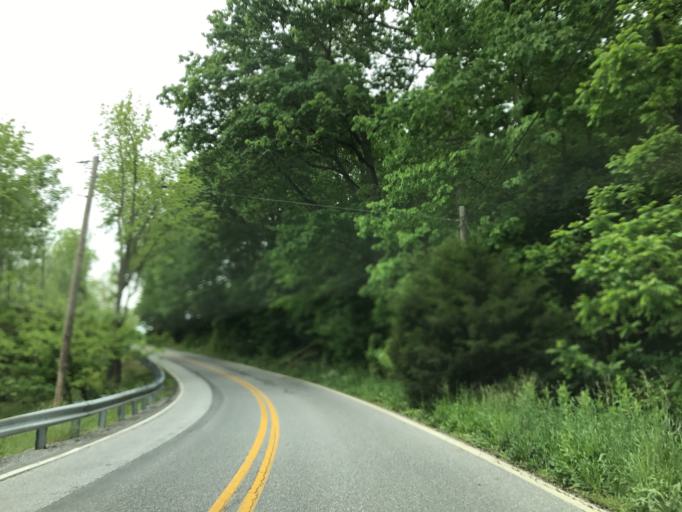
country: US
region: Pennsylvania
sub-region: York County
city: Dallastown
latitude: 39.8464
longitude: -76.6528
